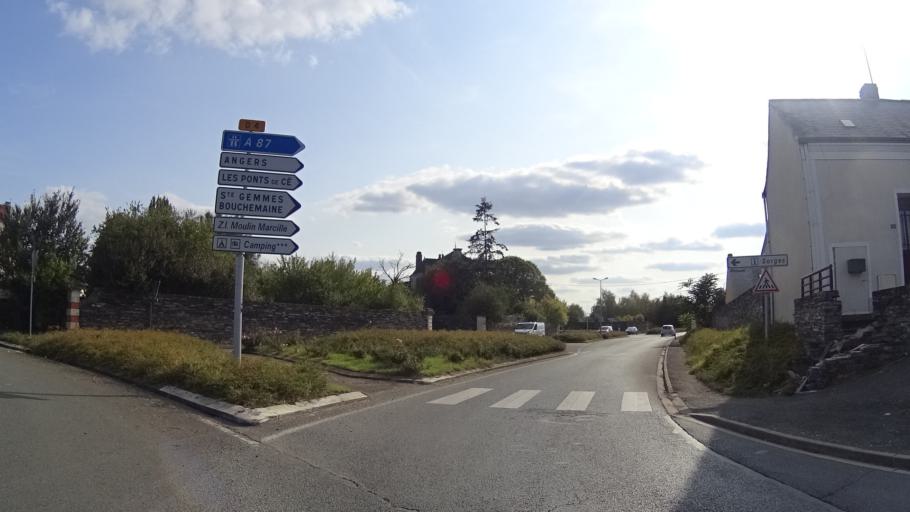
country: FR
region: Pays de la Loire
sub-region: Departement de Maine-et-Loire
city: Trelaze
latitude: 47.4391
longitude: -0.4865
